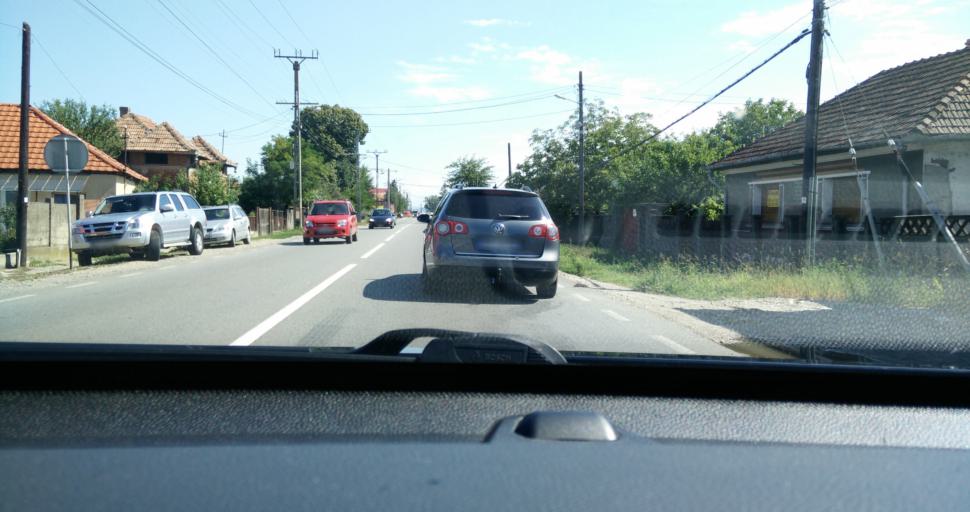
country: RO
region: Bihor
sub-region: Comuna Osorheiu
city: Osorheiu
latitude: 47.0456
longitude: 22.0368
